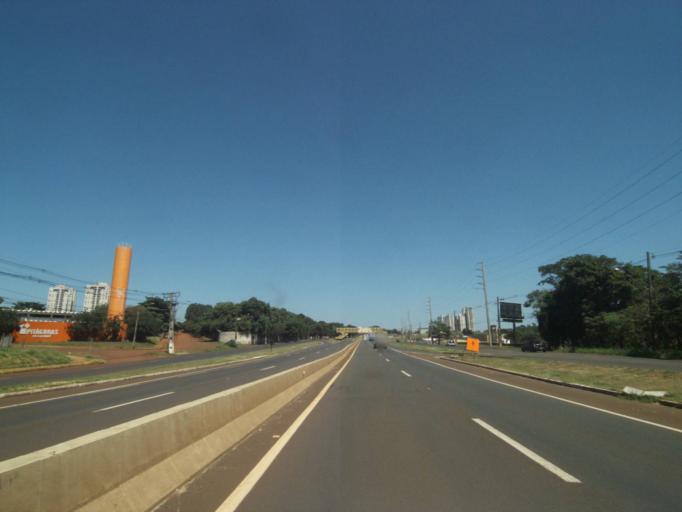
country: BR
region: Parana
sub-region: Londrina
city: Londrina
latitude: -23.3459
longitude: -51.1752
